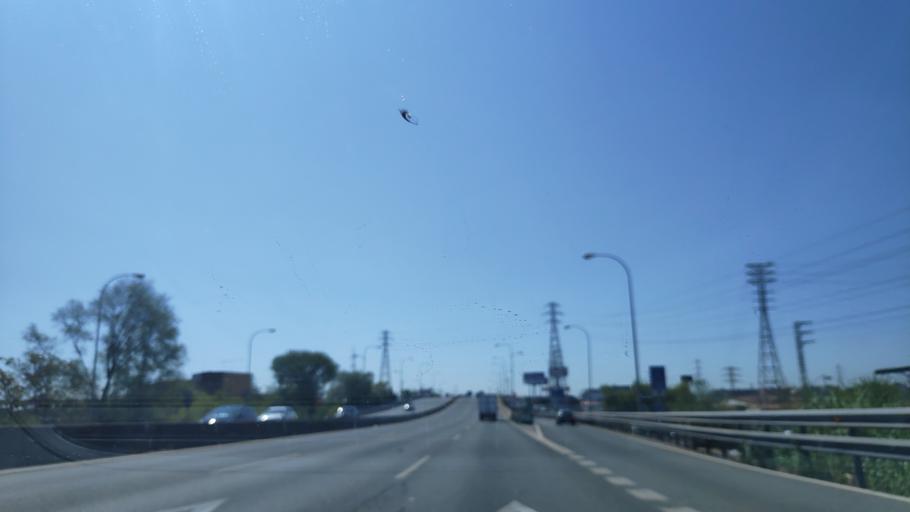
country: ES
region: Madrid
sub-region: Provincia de Madrid
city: Villaverde
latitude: 40.3402
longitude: -3.7242
